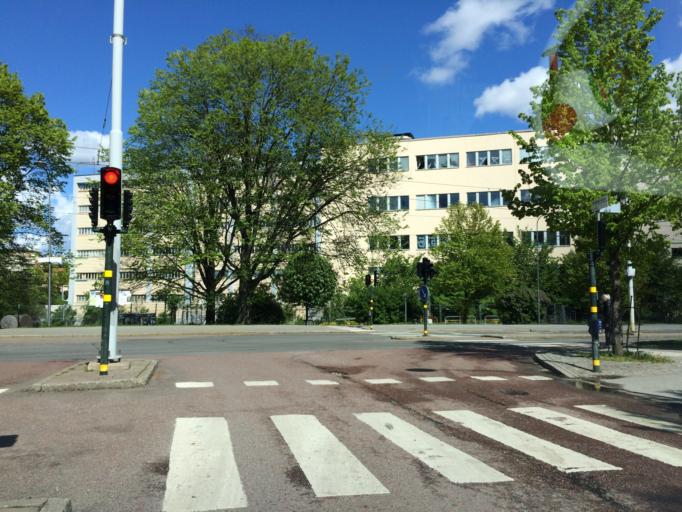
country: SE
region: Stockholm
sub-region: Stockholms Kommun
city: Arsta
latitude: 59.3143
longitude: 18.0163
